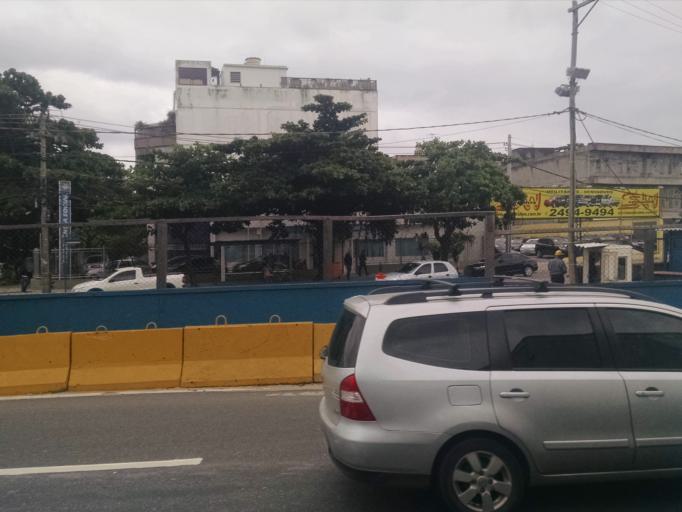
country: BR
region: Rio de Janeiro
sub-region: Rio De Janeiro
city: Rio de Janeiro
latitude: -23.0070
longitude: -43.3084
